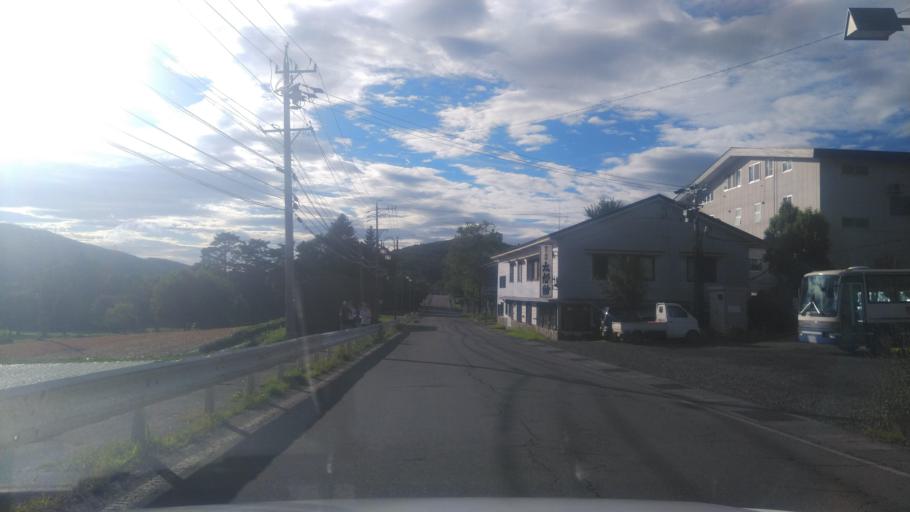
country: JP
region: Nagano
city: Suzaka
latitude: 36.5304
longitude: 138.3316
